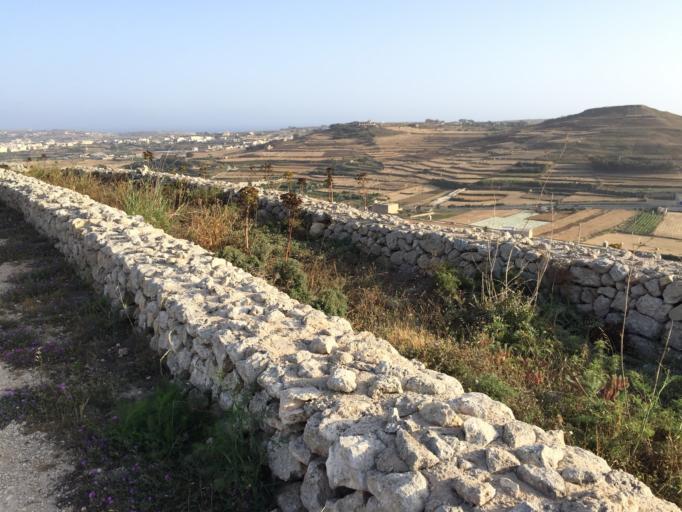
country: MT
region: L-Gharb
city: Gharb
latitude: 36.0587
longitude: 14.2192
